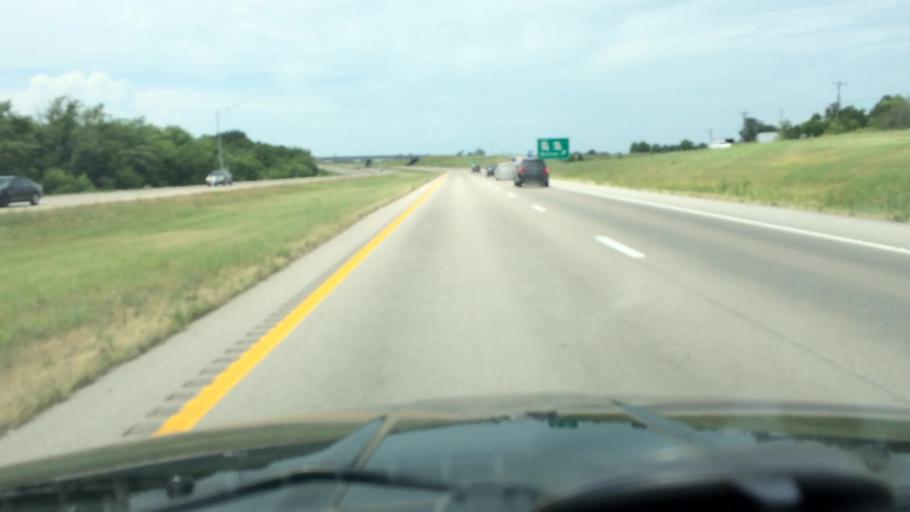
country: US
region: Missouri
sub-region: Polk County
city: Bolivar
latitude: 37.5700
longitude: -93.3959
